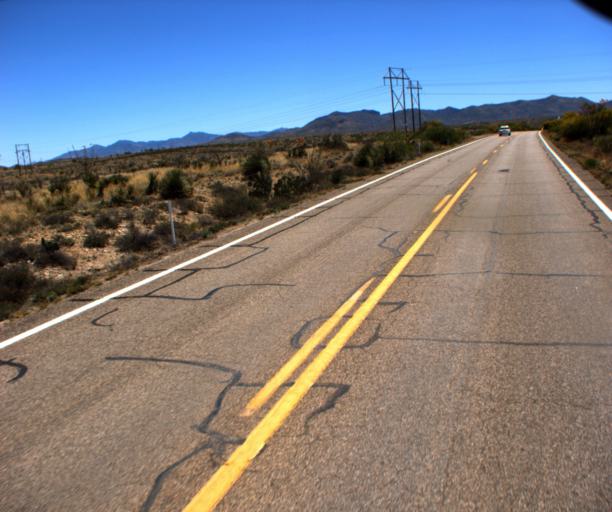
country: US
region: Arizona
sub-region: Pima County
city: Vail
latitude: 31.9922
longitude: -110.6840
